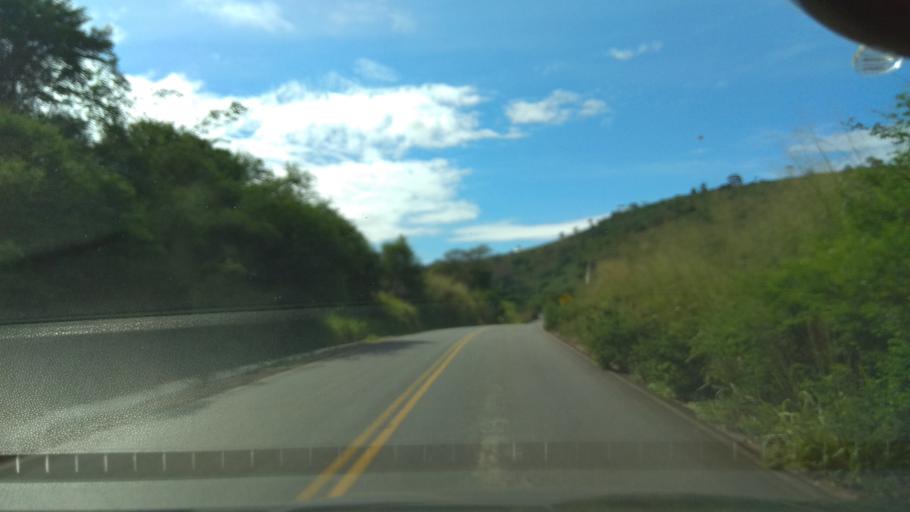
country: BR
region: Bahia
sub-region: Ubaira
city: Ubaira
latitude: -13.2632
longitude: -39.6817
